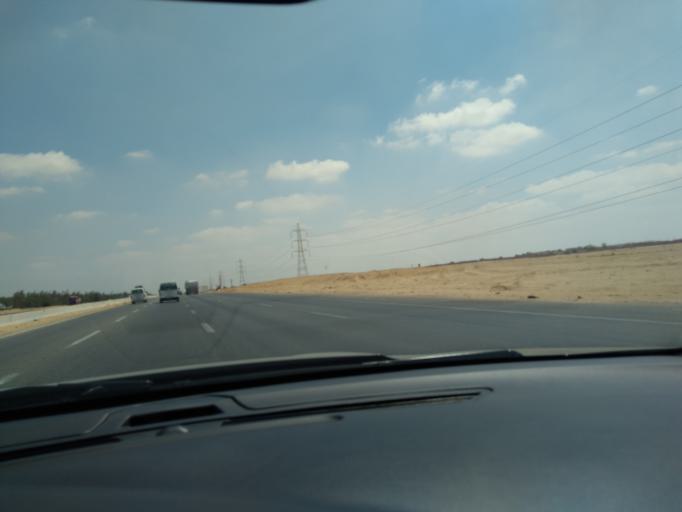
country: EG
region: Al Isma'iliyah
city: At Tall al Kabir
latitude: 30.3894
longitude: 31.9634
